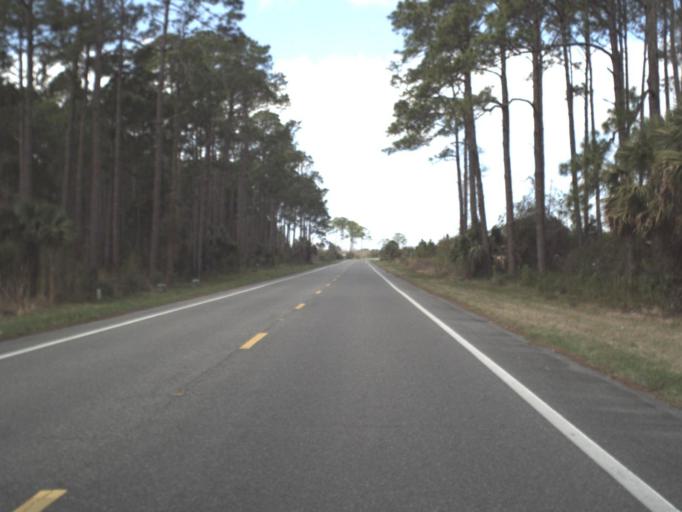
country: US
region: Florida
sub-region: Franklin County
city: Apalachicola
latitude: 29.7178
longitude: -85.0552
